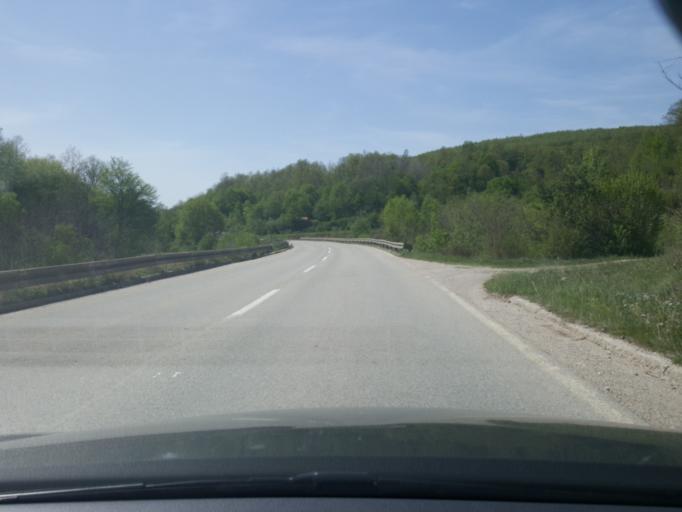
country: RS
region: Central Serbia
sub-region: Zlatiborski Okrug
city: Cajetina
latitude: 43.7883
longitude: 19.7198
